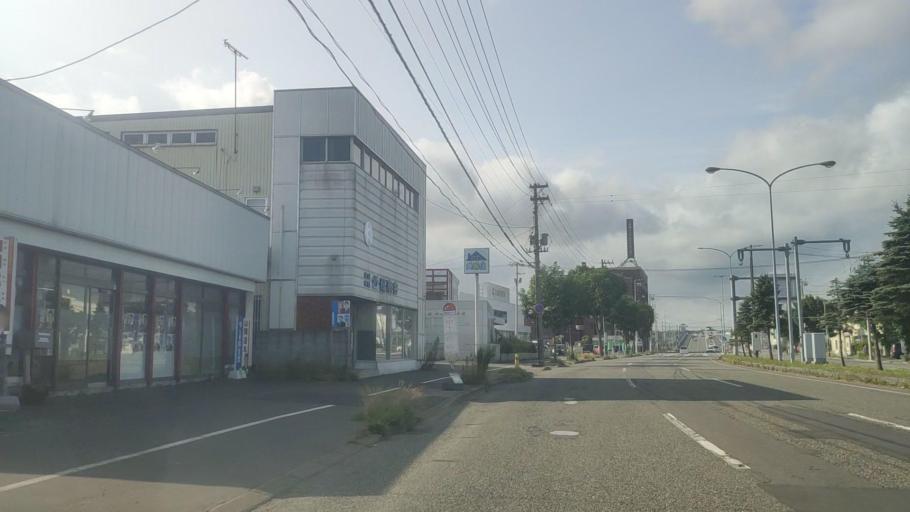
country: JP
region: Hokkaido
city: Tomakomai
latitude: 42.6398
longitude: 141.6109
